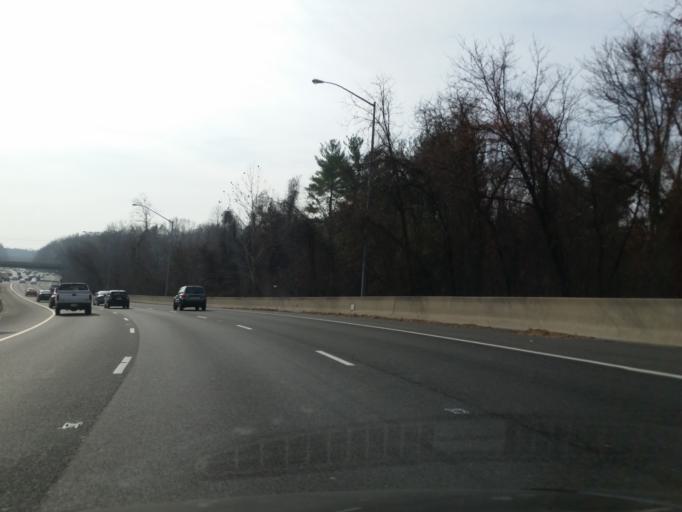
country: US
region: Maryland
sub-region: Montgomery County
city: Cabin John
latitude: 39.0123
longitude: -77.1502
